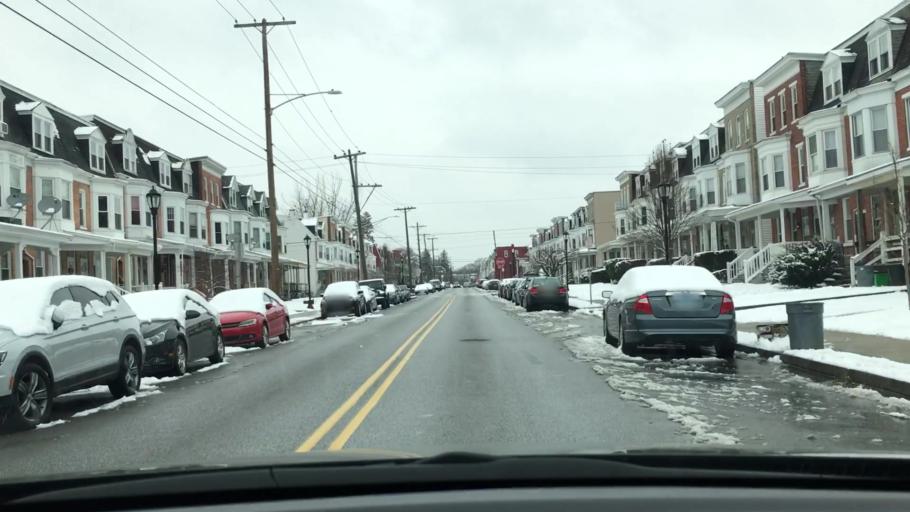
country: US
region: Pennsylvania
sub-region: York County
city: Grantley
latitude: 39.9504
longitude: -76.7289
